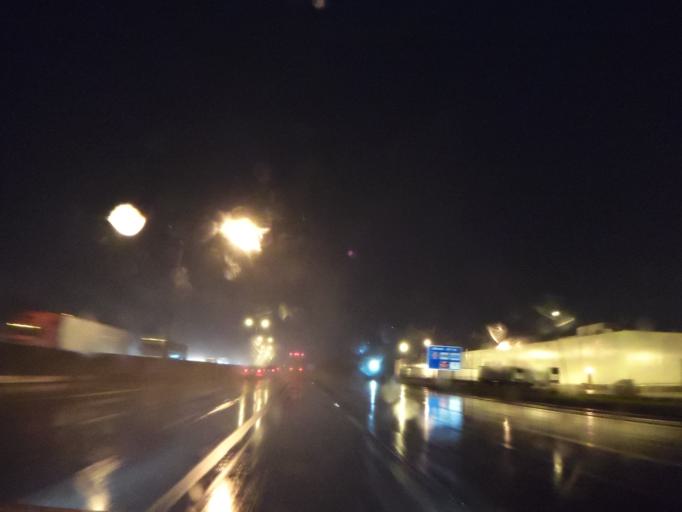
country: US
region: Kentucky
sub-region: Boone County
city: Florence
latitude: 38.9729
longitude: -84.6370
